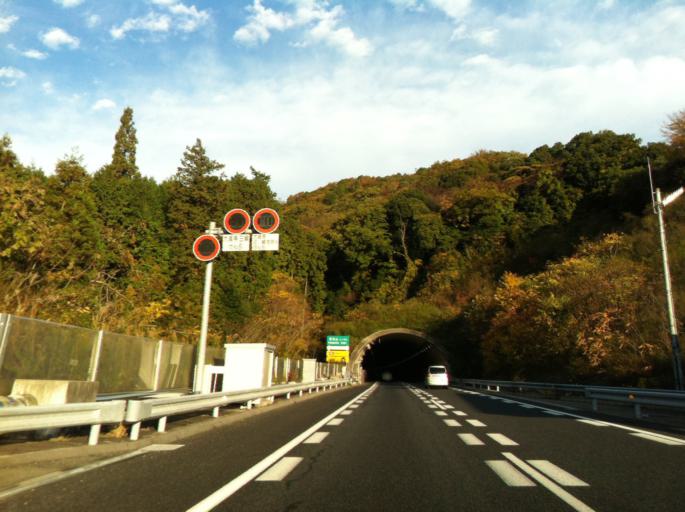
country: JP
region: Aichi
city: Seto
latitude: 35.1749
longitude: 137.1719
